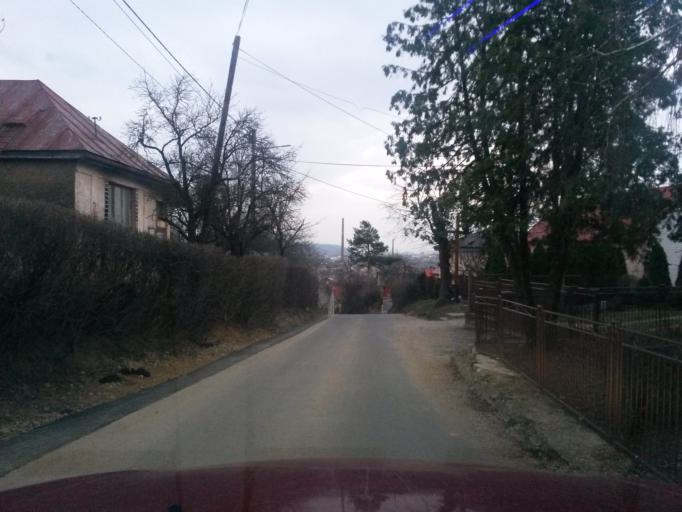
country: SK
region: Kosicky
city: Kosice
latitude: 48.7610
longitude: 21.2554
